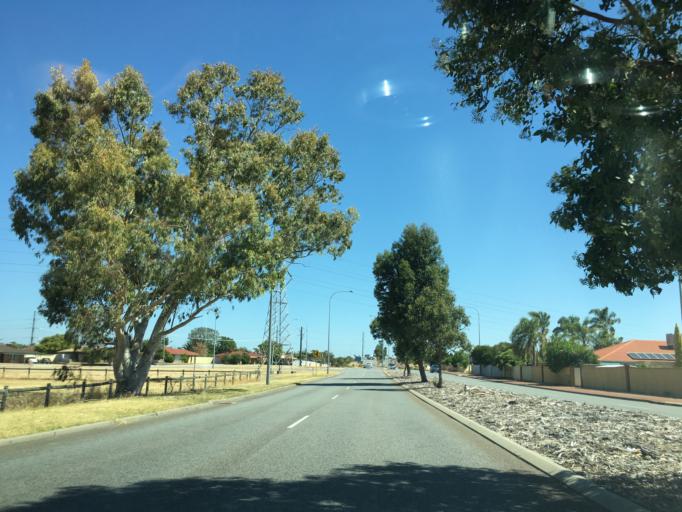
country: AU
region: Western Australia
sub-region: Canning
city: Canning Vale
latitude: -32.0526
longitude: 115.9044
